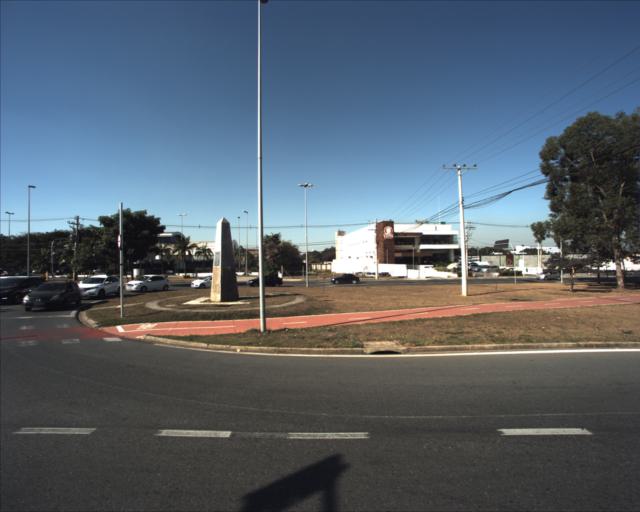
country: BR
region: Sao Paulo
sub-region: Sorocaba
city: Sorocaba
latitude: -23.4810
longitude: -47.4216
